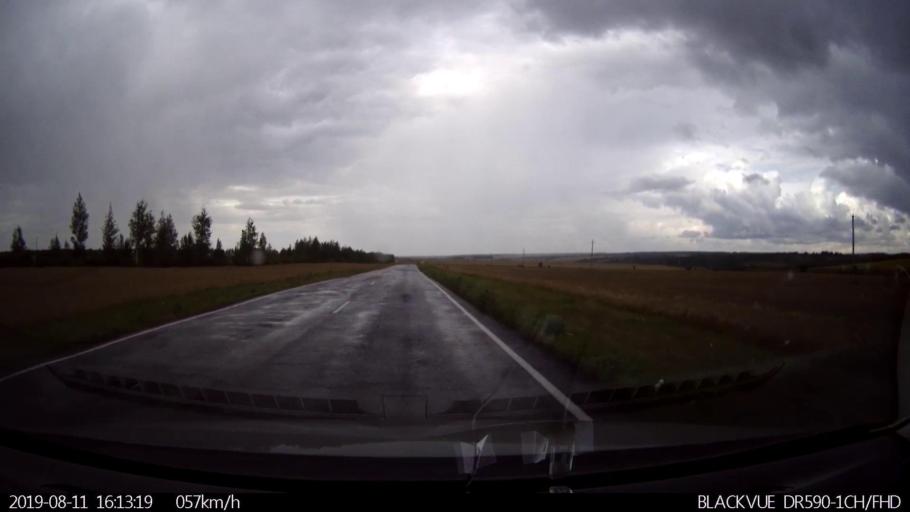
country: RU
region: Ulyanovsk
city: Ignatovka
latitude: 54.0191
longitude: 47.6373
